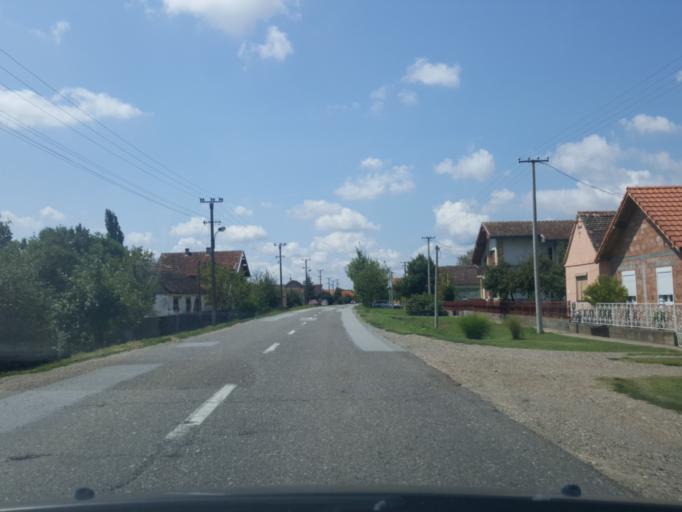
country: RS
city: Salas Nocajski
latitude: 44.9300
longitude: 19.5634
